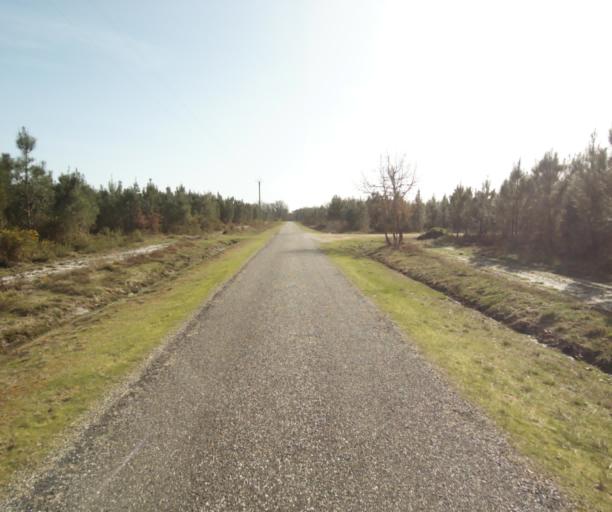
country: FR
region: Aquitaine
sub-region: Departement des Landes
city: Roquefort
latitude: 44.1321
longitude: -0.1936
